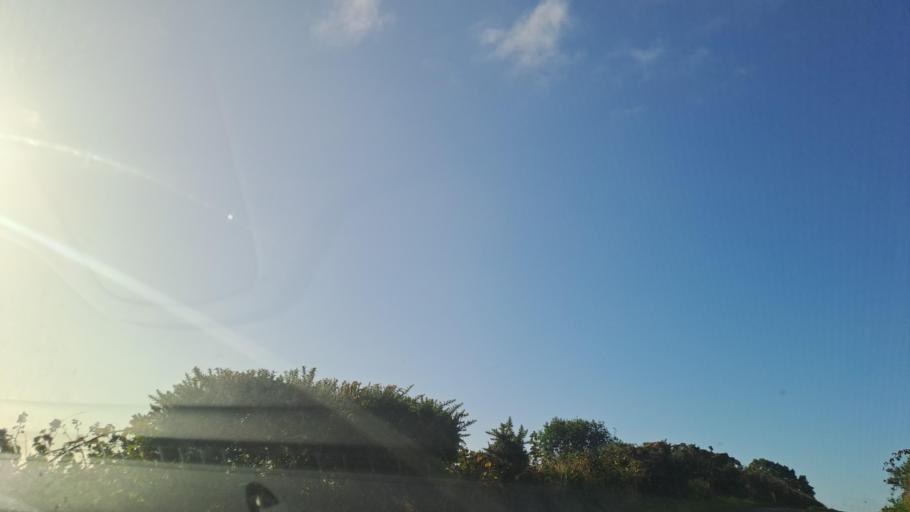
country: IE
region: Ulster
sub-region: An Cabhan
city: Kingscourt
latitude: 53.9614
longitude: -6.8627
